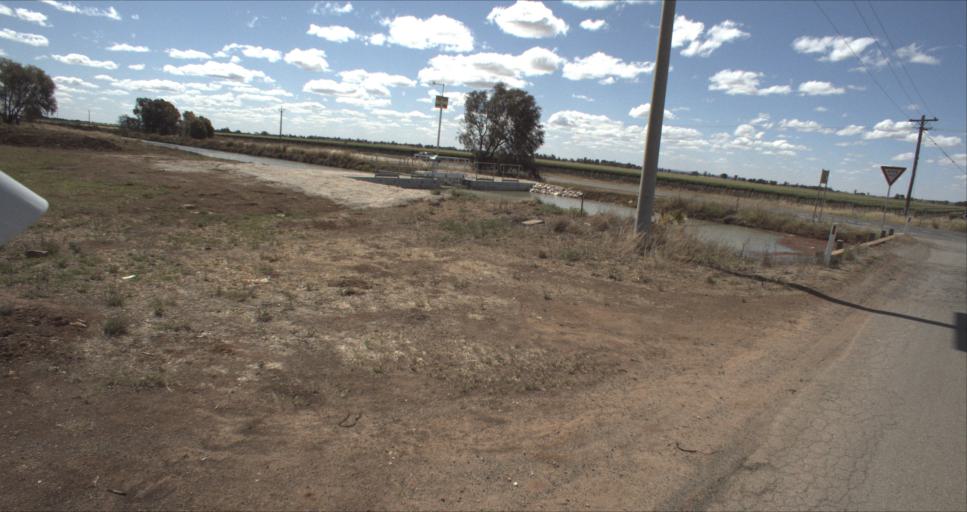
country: AU
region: New South Wales
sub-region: Leeton
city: Leeton
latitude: -34.5087
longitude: 146.2545
